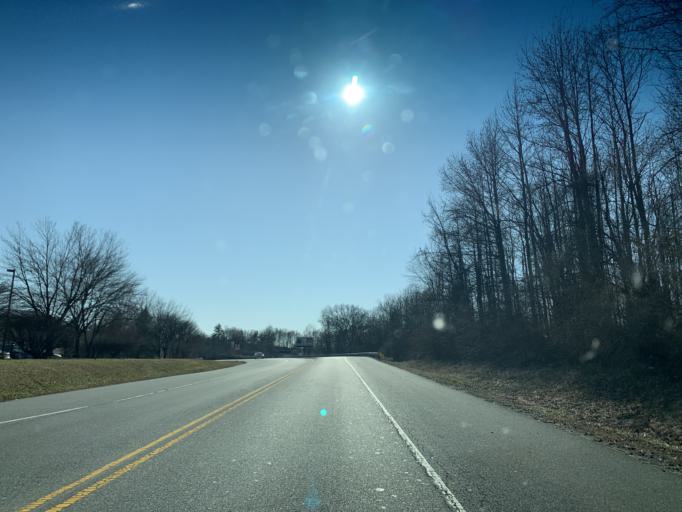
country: US
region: Maryland
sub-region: Cecil County
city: Elkton
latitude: 39.6098
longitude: -75.8522
